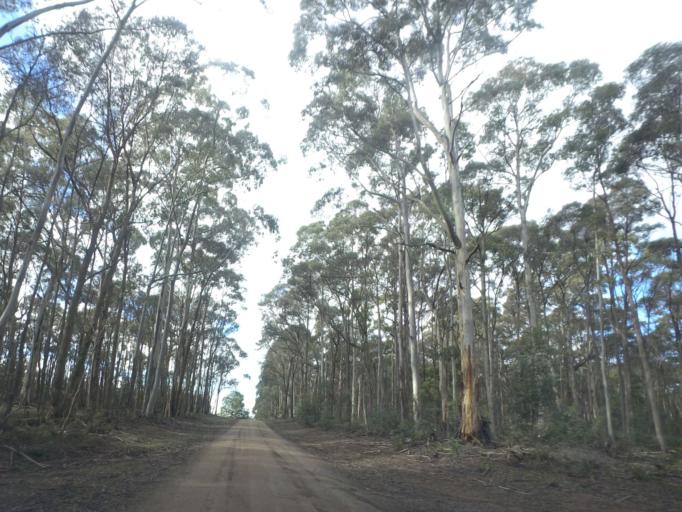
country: AU
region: Victoria
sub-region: Moorabool
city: Bacchus Marsh
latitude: -37.4303
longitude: 144.4364
